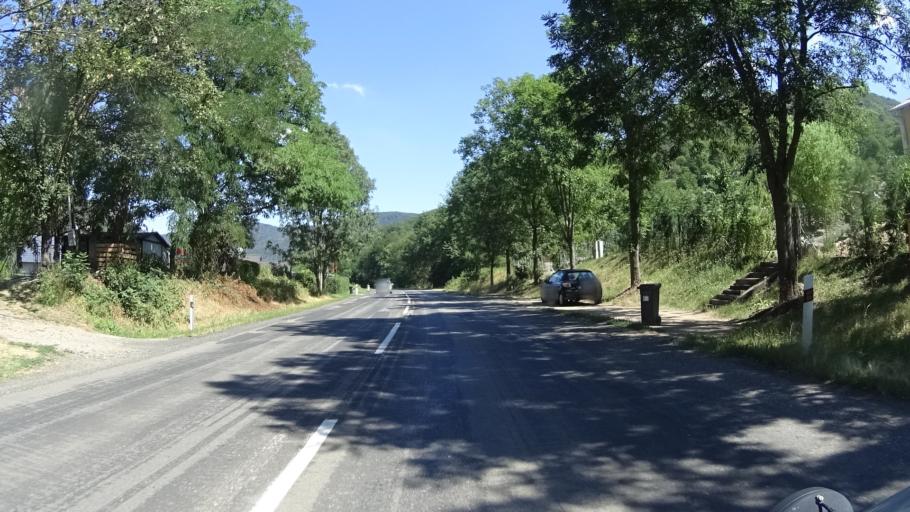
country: CZ
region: Ustecky
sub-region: Okres Usti nad Labem
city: Usti nad Labem
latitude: 50.5991
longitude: 14.0733
